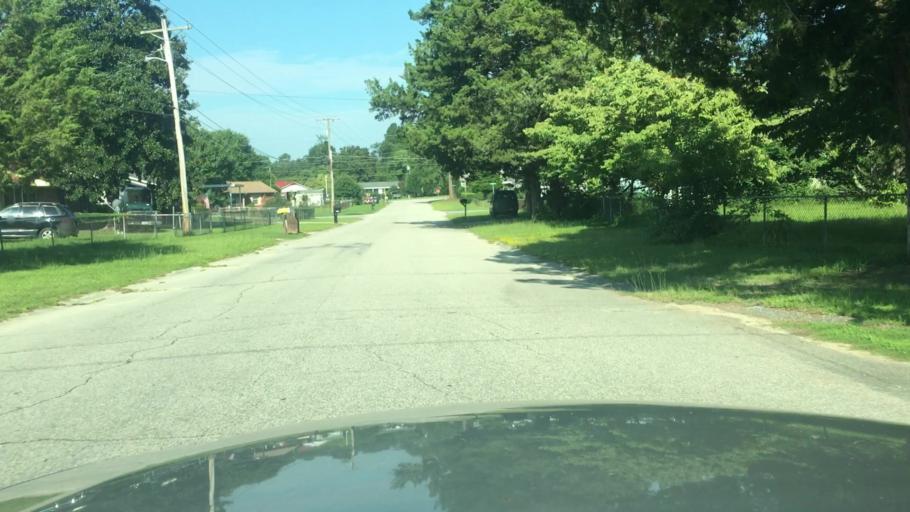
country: US
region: North Carolina
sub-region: Cumberland County
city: Spring Lake
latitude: 35.1535
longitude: -78.9173
